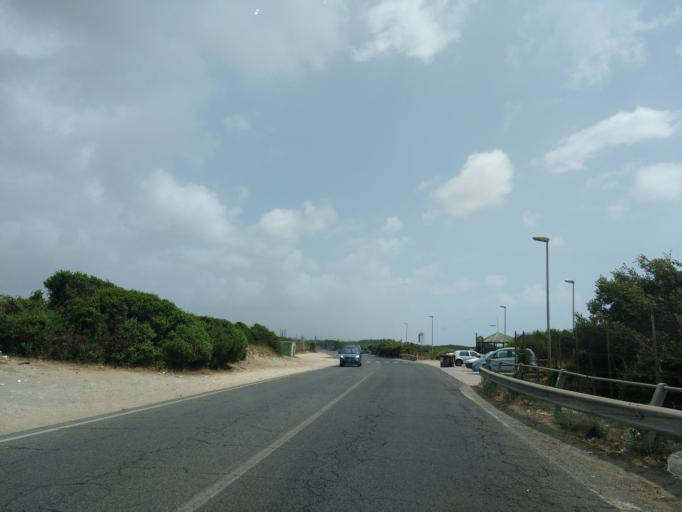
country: IT
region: Latium
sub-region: Citta metropolitana di Roma Capitale
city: Torvaianica
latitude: 41.6613
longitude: 12.4101
